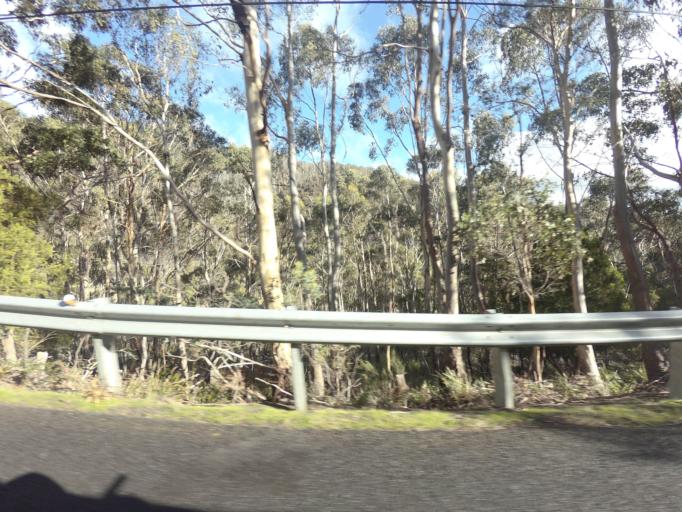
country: AU
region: Tasmania
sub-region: Glenorchy
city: Berriedale
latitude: -42.8112
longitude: 147.1717
